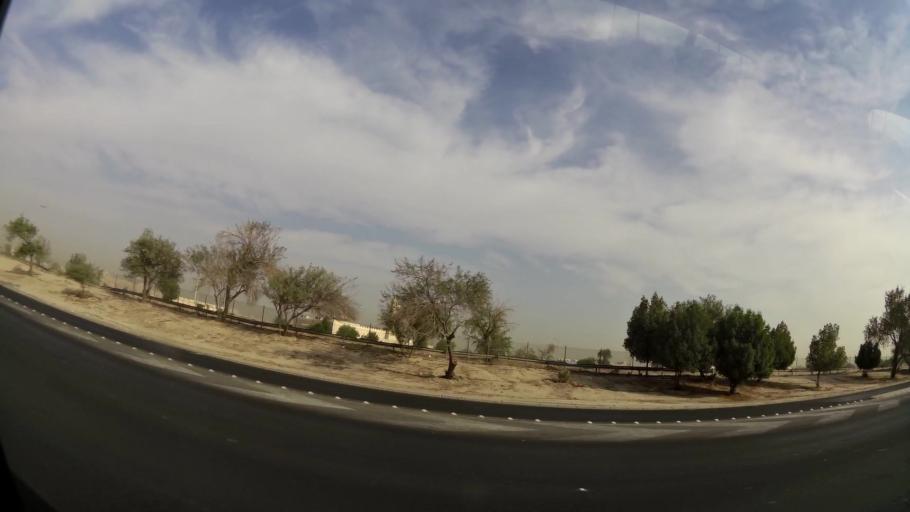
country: KW
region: Al Farwaniyah
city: Janub as Surrah
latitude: 29.2660
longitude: 47.9822
